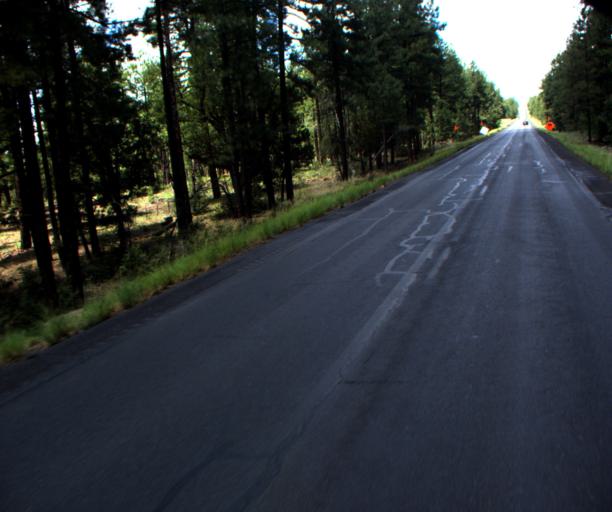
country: US
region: Arizona
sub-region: Gila County
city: Pine
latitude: 34.4771
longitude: -111.4515
